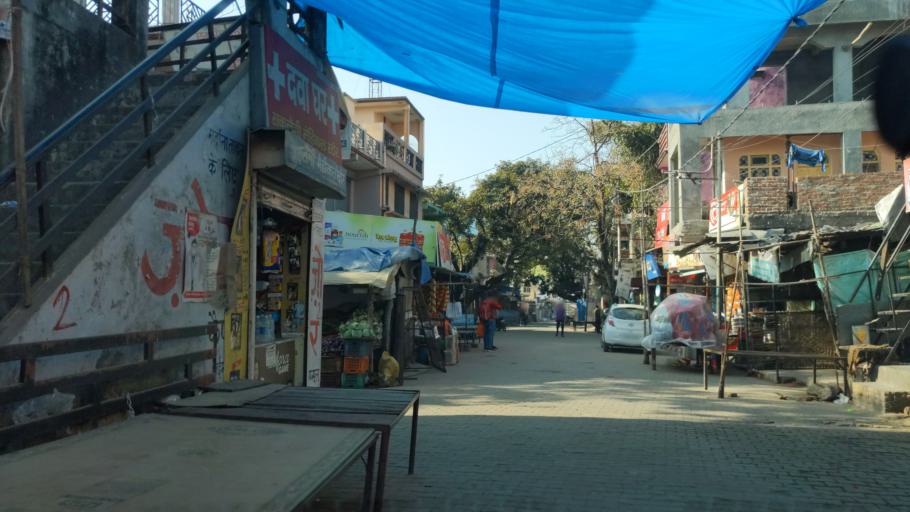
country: IN
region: Uttarakhand
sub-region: Naini Tal
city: Kaladhungi
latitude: 29.2831
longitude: 79.3490
